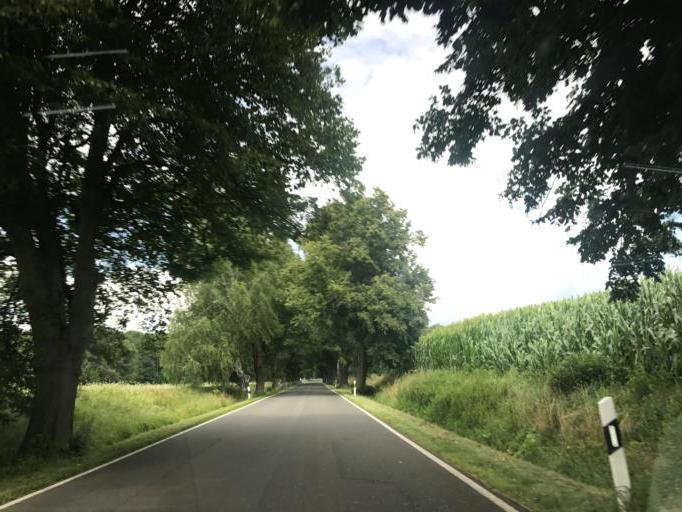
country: DE
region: Mecklenburg-Vorpommern
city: Wesenberg
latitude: 53.2083
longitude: 12.9181
